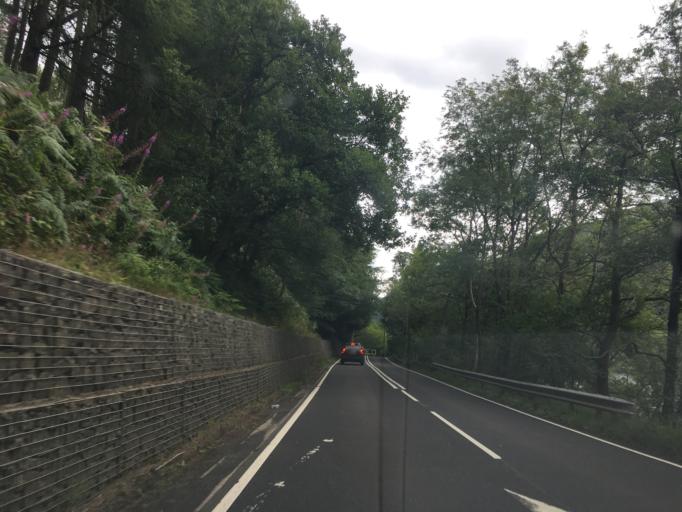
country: GB
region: Scotland
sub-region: Stirling
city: Callander
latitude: 56.3037
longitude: -4.3180
